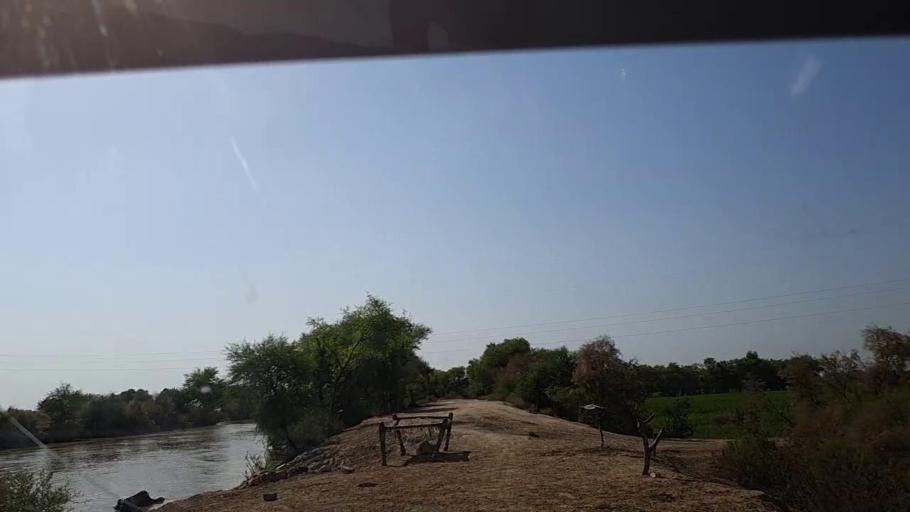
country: PK
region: Sindh
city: Ghauspur
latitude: 28.1842
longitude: 69.0806
